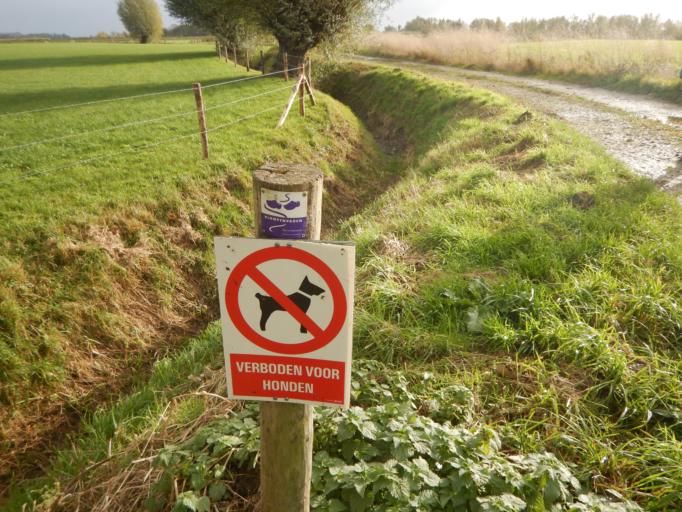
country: NL
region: Gelderland
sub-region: Gemeente Zevenaar
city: Zevenaar
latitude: 51.9124
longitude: 6.0831
